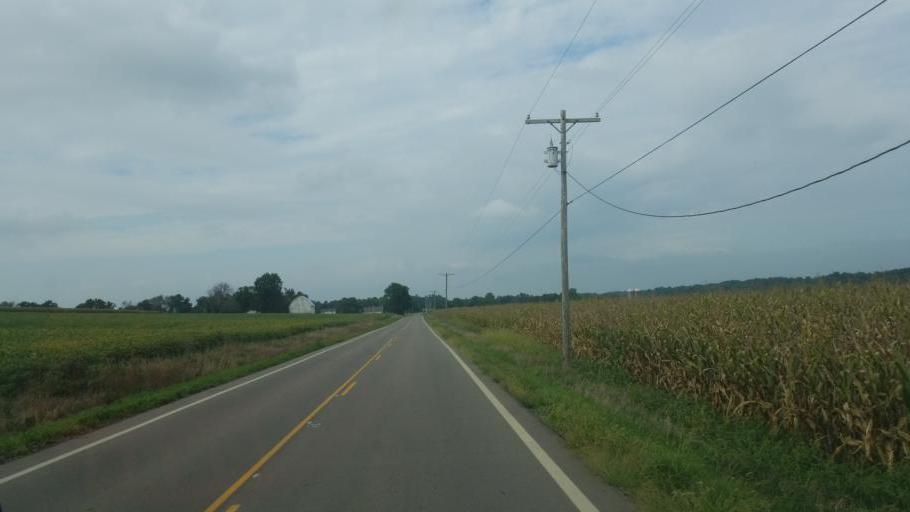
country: US
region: Ohio
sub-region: Wayne County
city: West Salem
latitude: 40.8949
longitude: -82.0527
